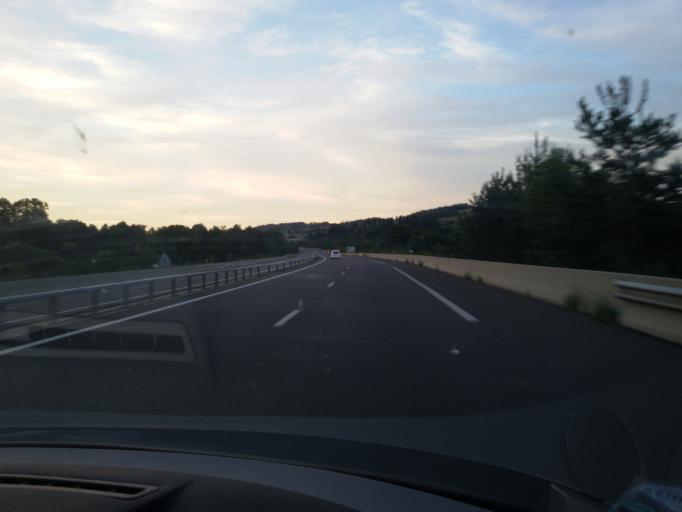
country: FR
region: Languedoc-Roussillon
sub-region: Departement de la Lozere
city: Marvejols
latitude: 44.6123
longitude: 3.2580
